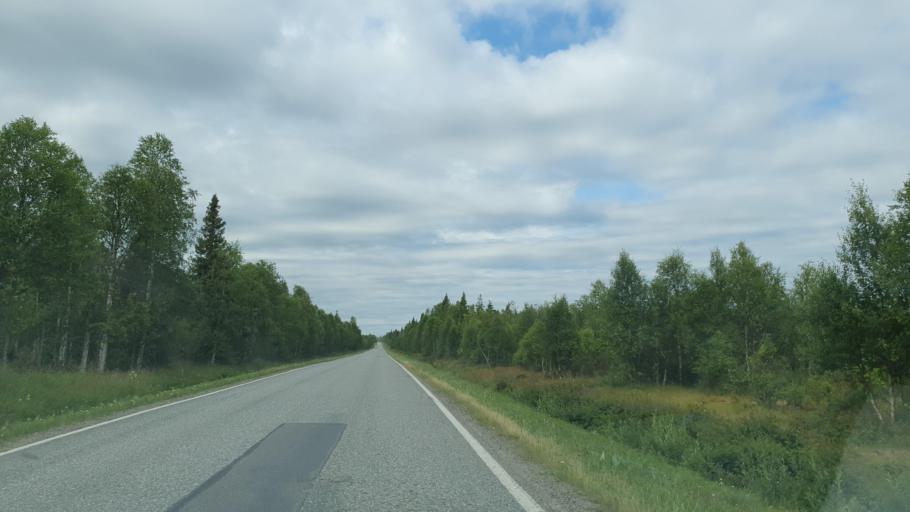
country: FI
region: Lapland
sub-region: Tunturi-Lappi
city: Kittilae
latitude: 67.6154
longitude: 25.3717
